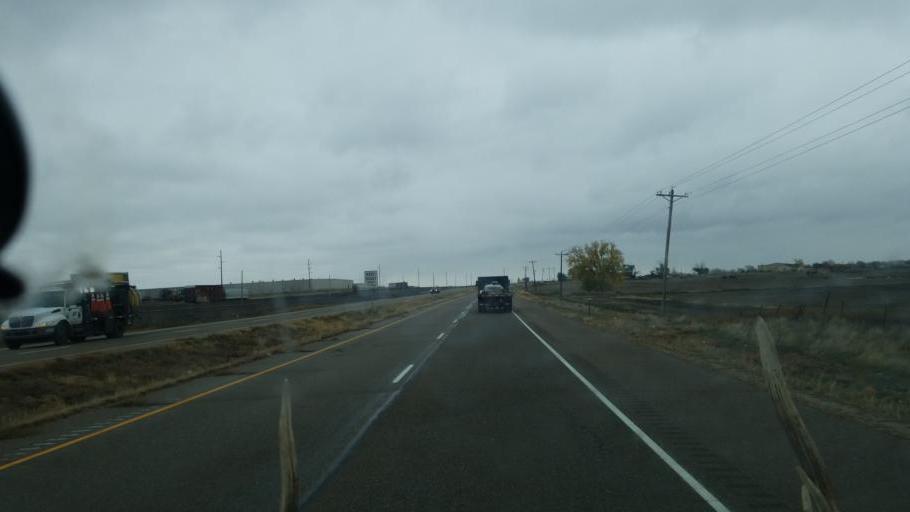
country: US
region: Colorado
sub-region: Pueblo County
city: Pueblo
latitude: 38.2756
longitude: -104.4766
